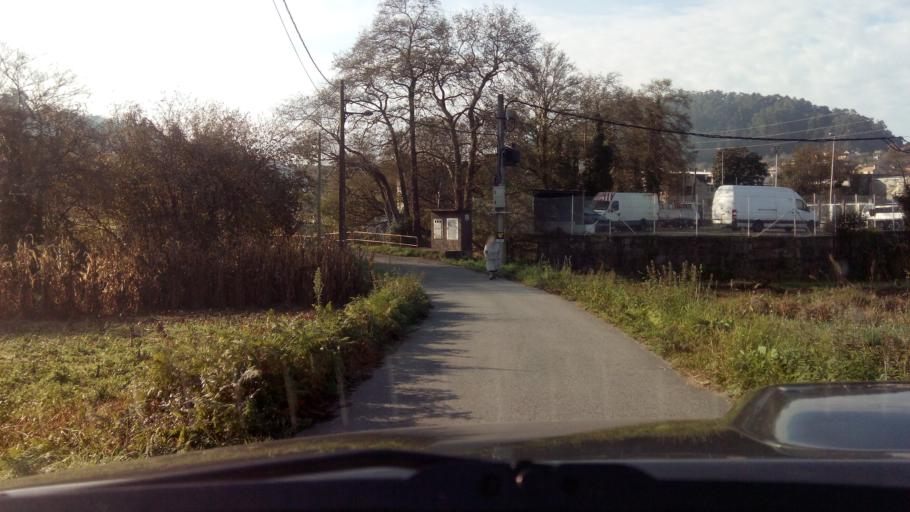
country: ES
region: Galicia
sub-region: Provincia de Pontevedra
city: Marin
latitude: 42.3636
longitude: -8.7362
